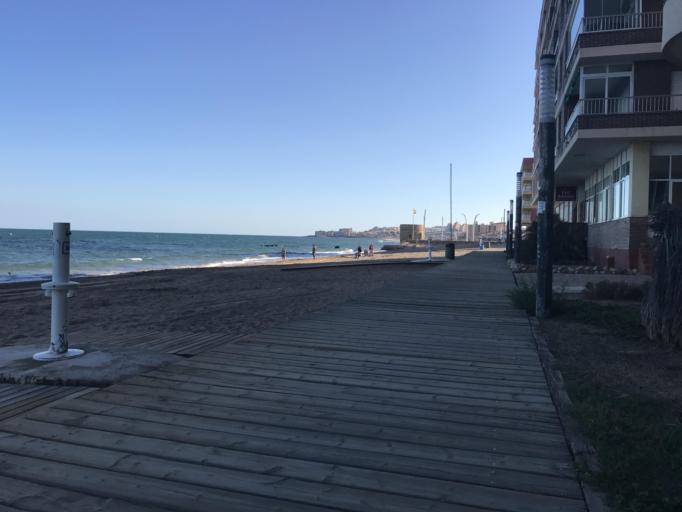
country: ES
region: Valencia
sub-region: Provincia de Alicante
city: Torrevieja
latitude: 38.0278
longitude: -0.6525
